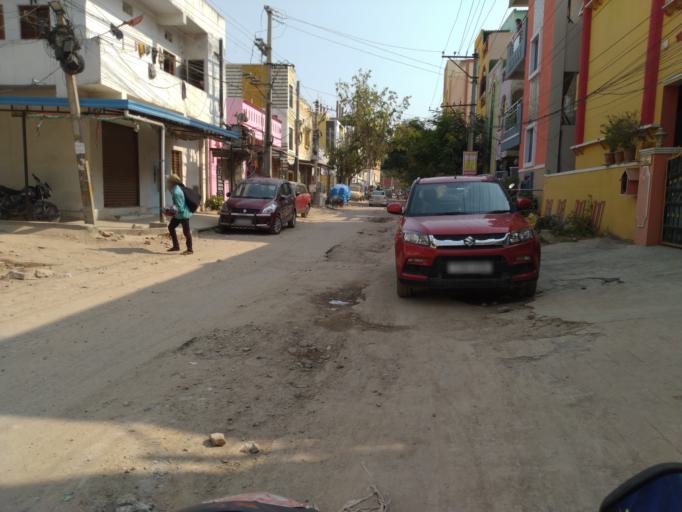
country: IN
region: Telangana
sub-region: Rangareddi
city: Quthbullapur
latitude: 17.4970
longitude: 78.4644
